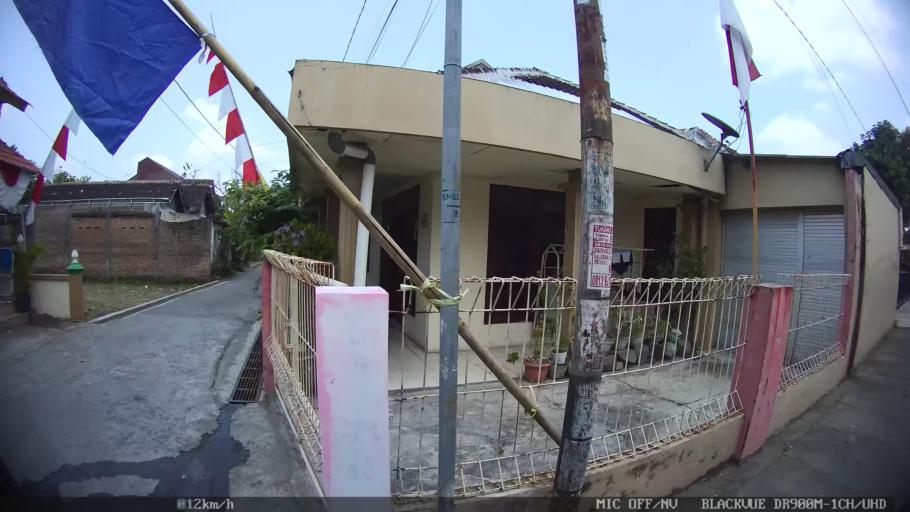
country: ID
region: Daerah Istimewa Yogyakarta
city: Yogyakarta
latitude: -7.8166
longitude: 110.3896
